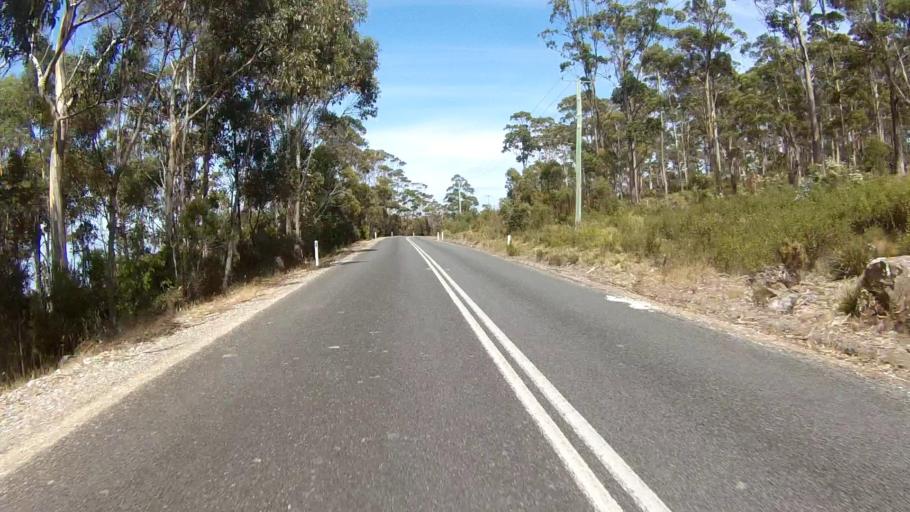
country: AU
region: Tasmania
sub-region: Huon Valley
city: Cygnet
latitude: -43.2815
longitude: 147.1727
